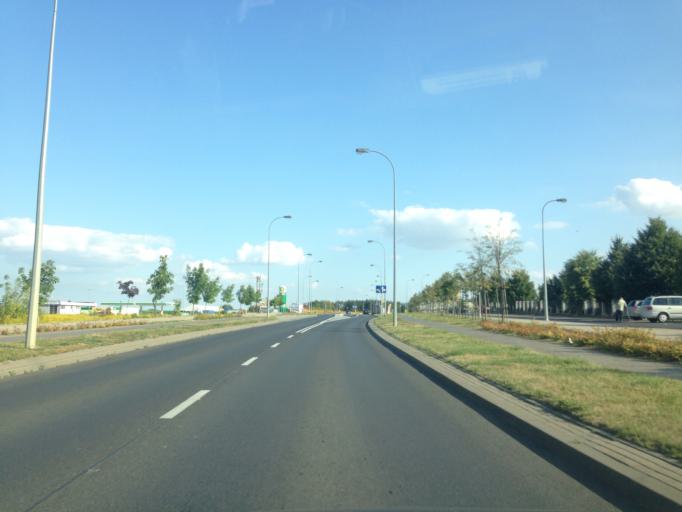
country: PL
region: Warmian-Masurian Voivodeship
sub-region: Powiat ilawski
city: Ilawa
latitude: 53.5954
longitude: 19.5803
